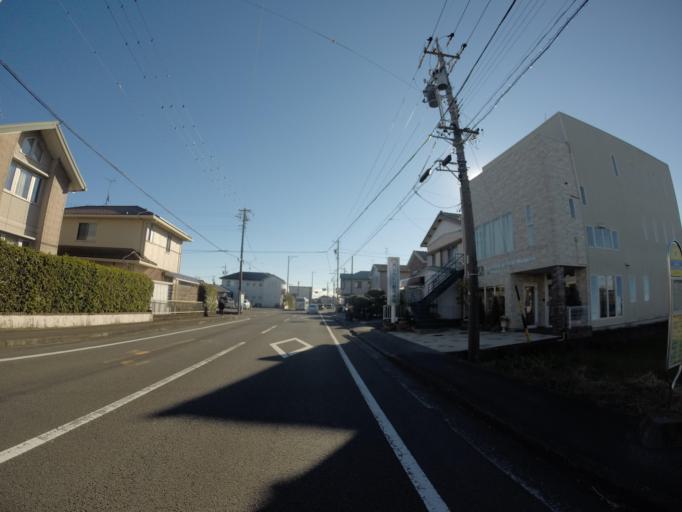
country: JP
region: Shizuoka
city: Fujieda
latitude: 34.8289
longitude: 138.2577
